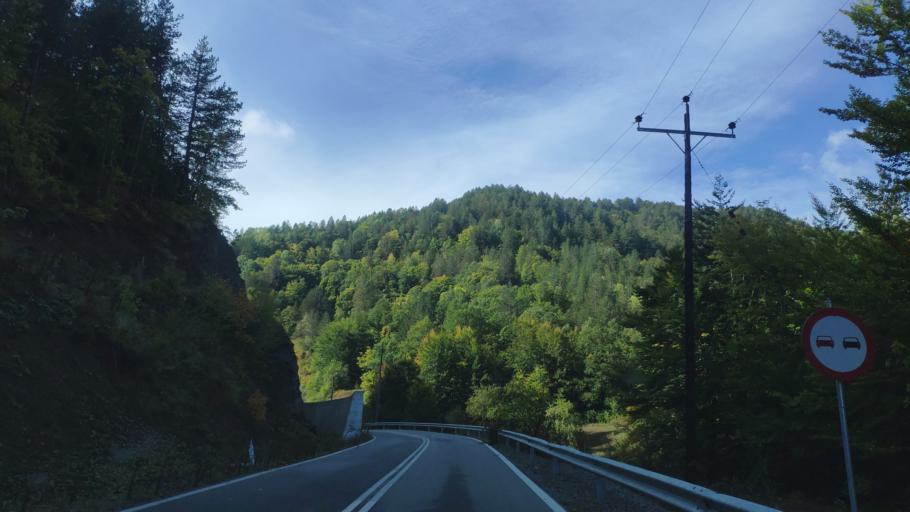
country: GR
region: West Macedonia
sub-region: Nomos Kastorias
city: Nestorio
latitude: 40.3810
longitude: 20.9426
